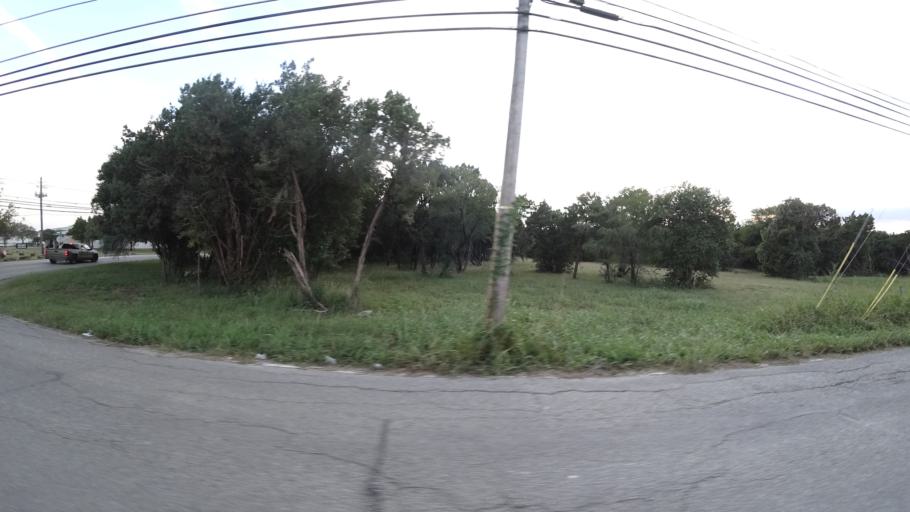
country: US
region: Texas
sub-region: Travis County
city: Austin
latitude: 30.2118
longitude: -97.7588
